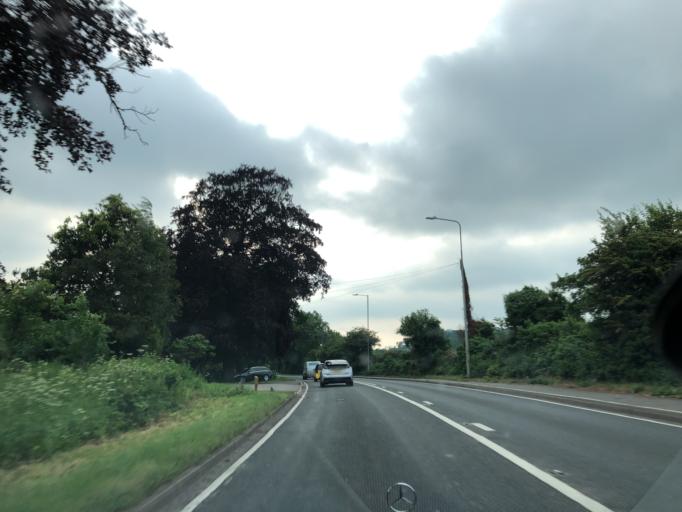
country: GB
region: England
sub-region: Warwickshire
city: Warwick
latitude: 52.2944
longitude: -1.6211
